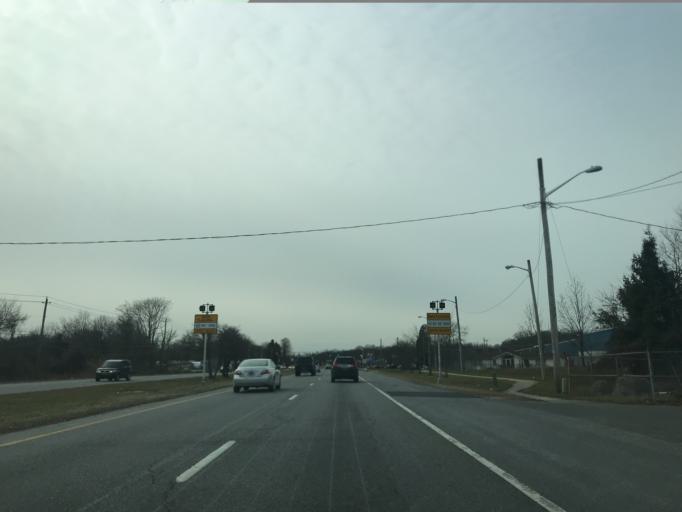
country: US
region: Delaware
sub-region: New Castle County
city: Bear
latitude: 39.6211
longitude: -75.6884
